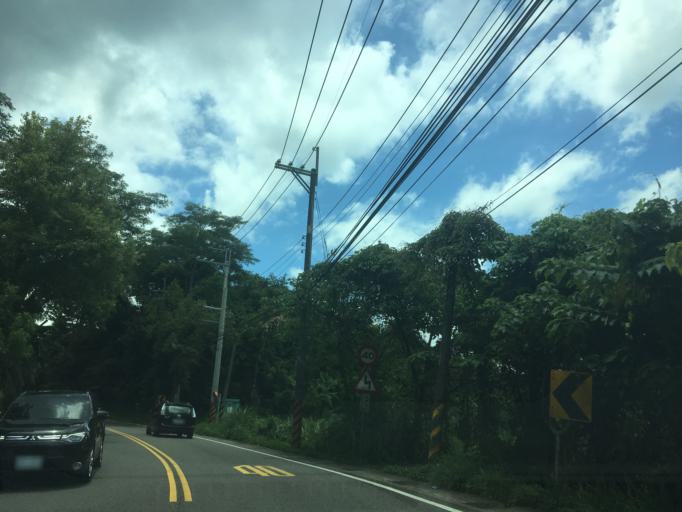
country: TW
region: Taiwan
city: Daxi
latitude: 24.8286
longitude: 121.3361
